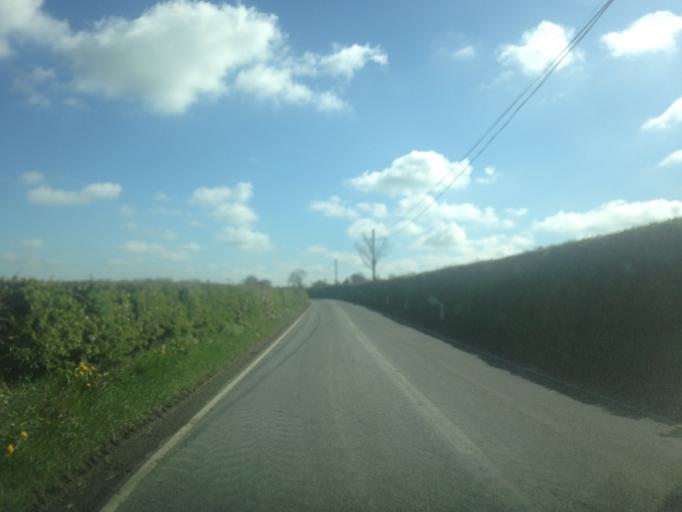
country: GB
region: Wales
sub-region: County of Ceredigion
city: Newcastle Emlyn
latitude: 52.0559
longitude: -4.4494
